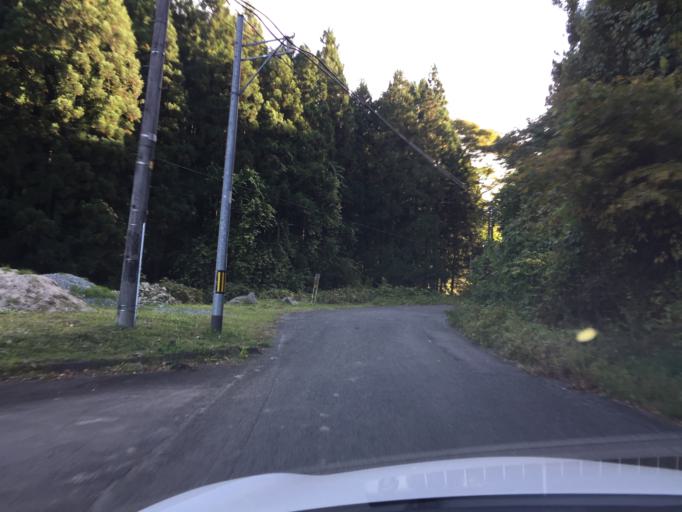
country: JP
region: Fukushima
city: Ishikawa
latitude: 37.2463
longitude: 140.6083
